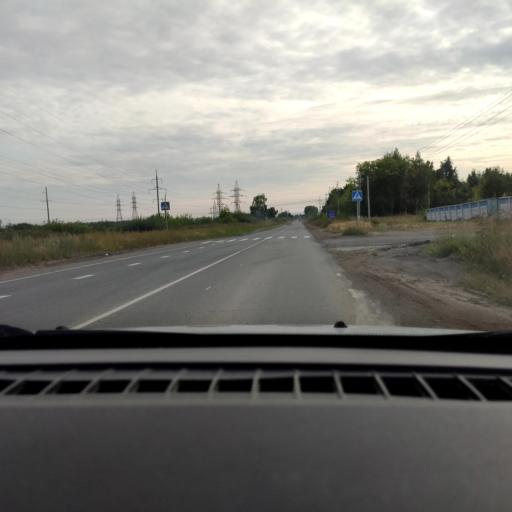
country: RU
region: Perm
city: Gamovo
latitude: 57.8871
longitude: 56.1676
